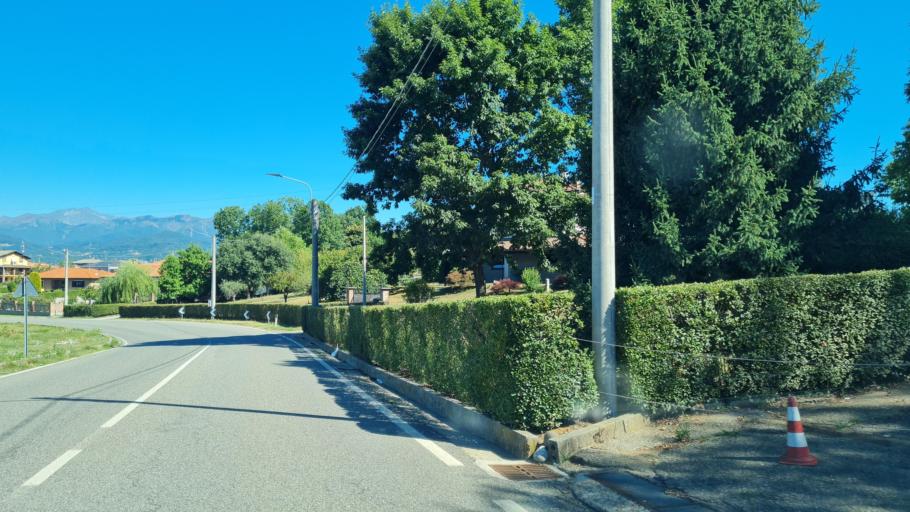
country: IT
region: Piedmont
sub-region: Provincia di Biella
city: Cossato
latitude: 45.5614
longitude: 8.1997
